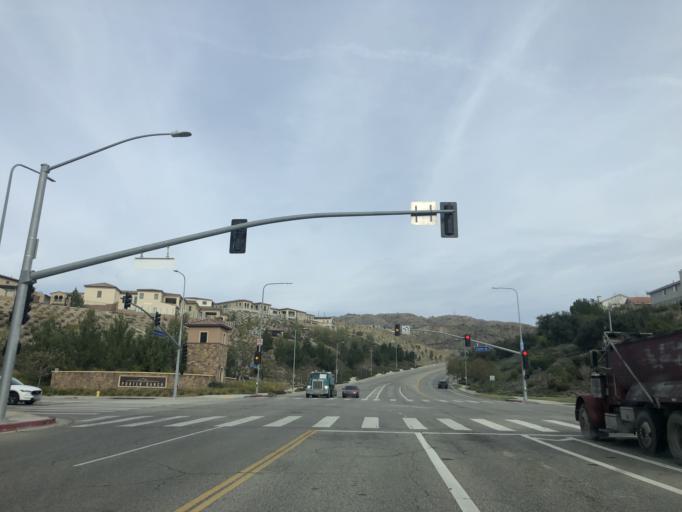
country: US
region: California
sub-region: Los Angeles County
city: Chatsworth
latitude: 34.2811
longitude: -118.5713
